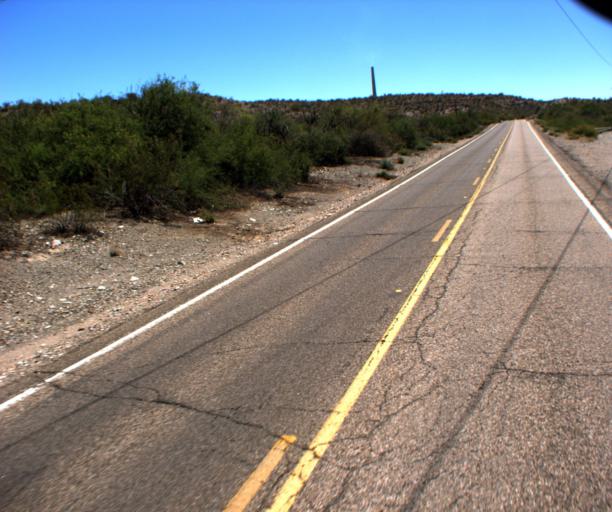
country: US
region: Arizona
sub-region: Pinal County
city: Kearny
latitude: 33.0093
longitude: -110.8053
